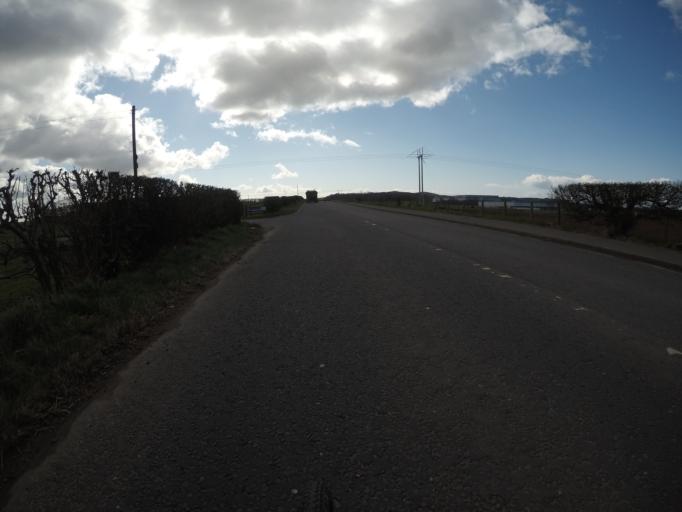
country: GB
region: Scotland
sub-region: North Ayrshire
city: Dreghorn
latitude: 55.5923
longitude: -4.6025
